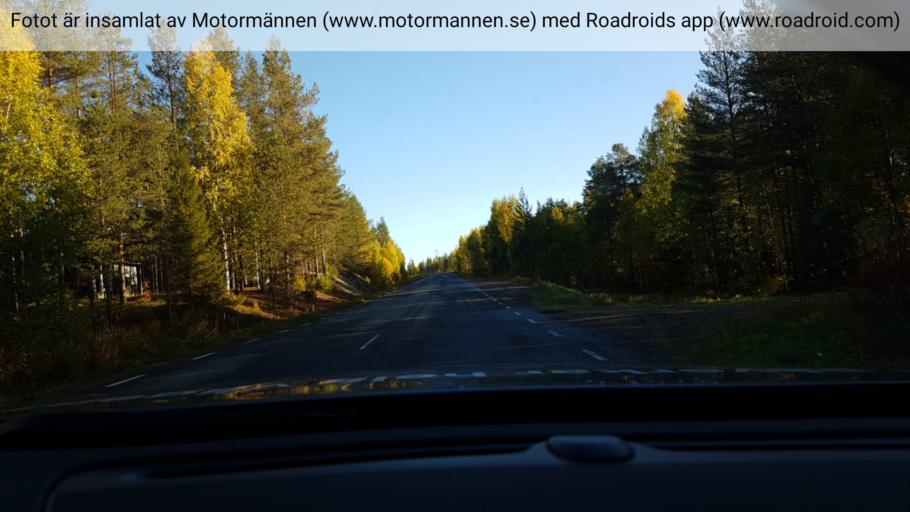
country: SE
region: Norrbotten
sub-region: Bodens Kommun
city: Boden
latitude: 65.9669
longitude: 21.6082
